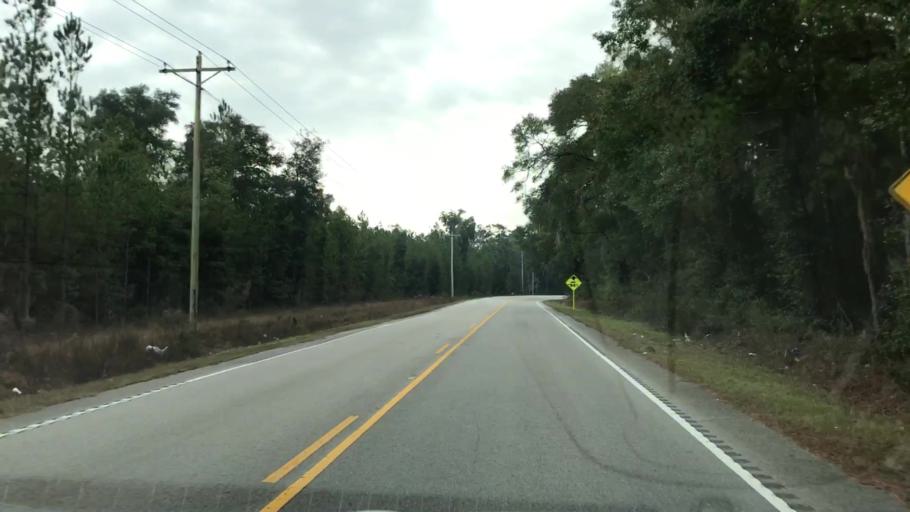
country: US
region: South Carolina
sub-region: Jasper County
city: Ridgeland
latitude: 32.4983
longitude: -80.8853
